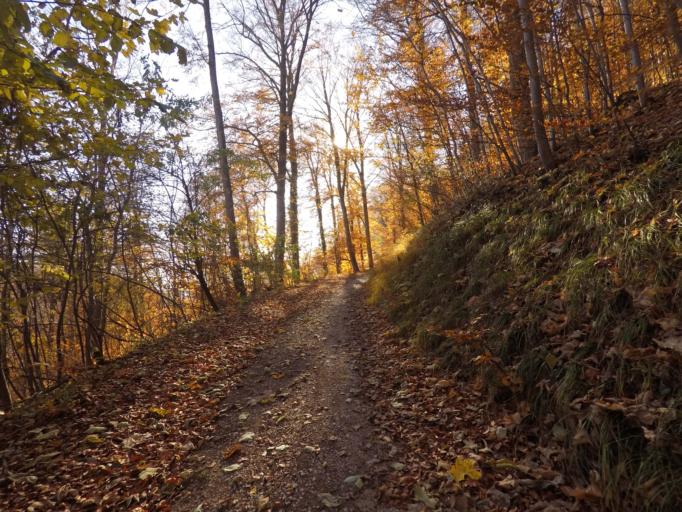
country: DE
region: Baden-Wuerttemberg
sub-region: Tuebingen Region
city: Pfullingen
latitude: 48.4416
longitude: 9.2293
